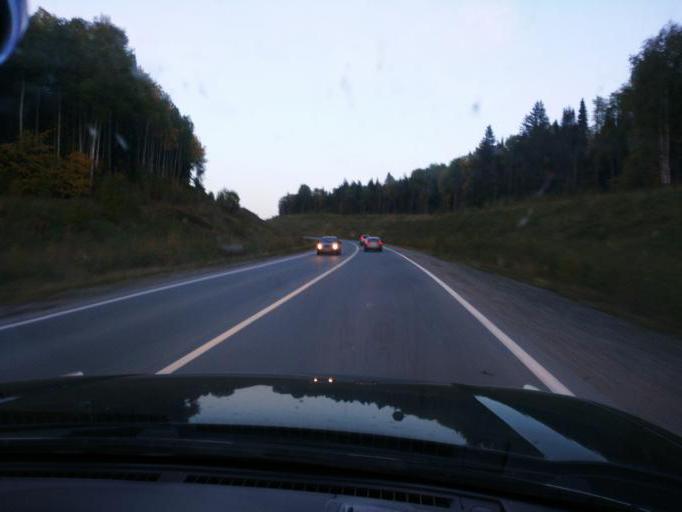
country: RU
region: Perm
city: Sylva
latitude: 58.2963
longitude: 56.8031
